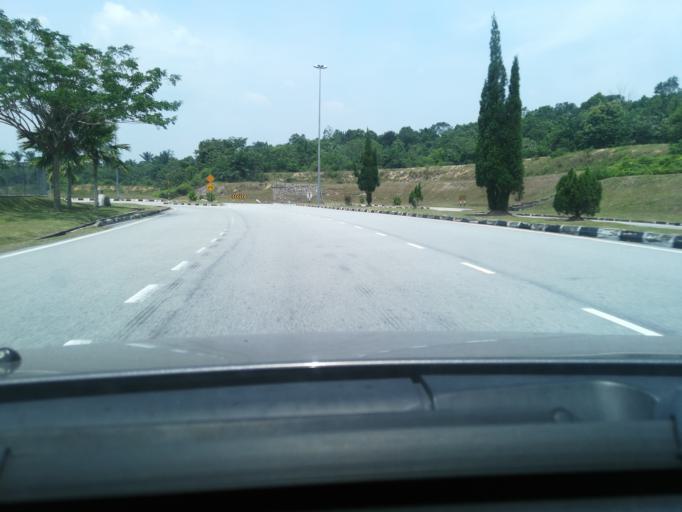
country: MY
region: Kedah
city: Kulim
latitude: 5.4223
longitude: 100.5776
